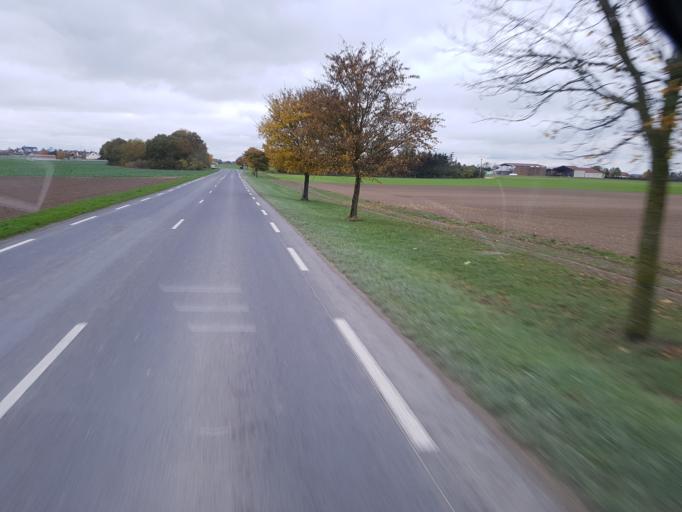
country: FR
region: Champagne-Ardenne
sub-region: Departement de la Marne
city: Saint-Just-Sauvage
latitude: 48.5870
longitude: 3.8316
